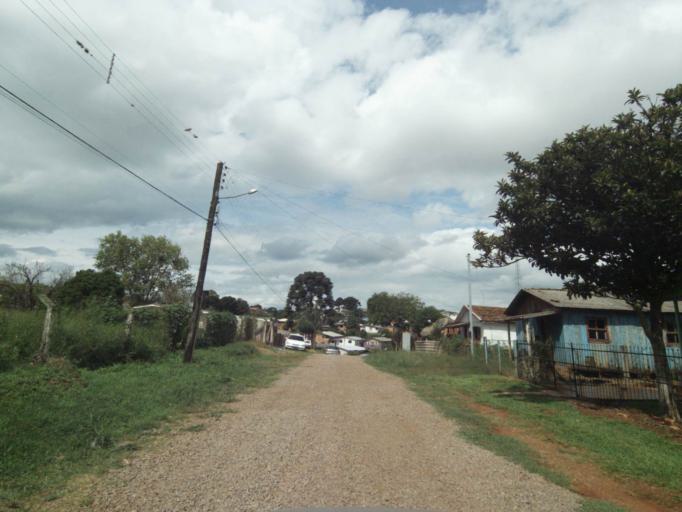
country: BR
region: Rio Grande do Sul
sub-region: Lagoa Vermelha
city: Lagoa Vermelha
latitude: -28.2095
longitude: -51.5409
